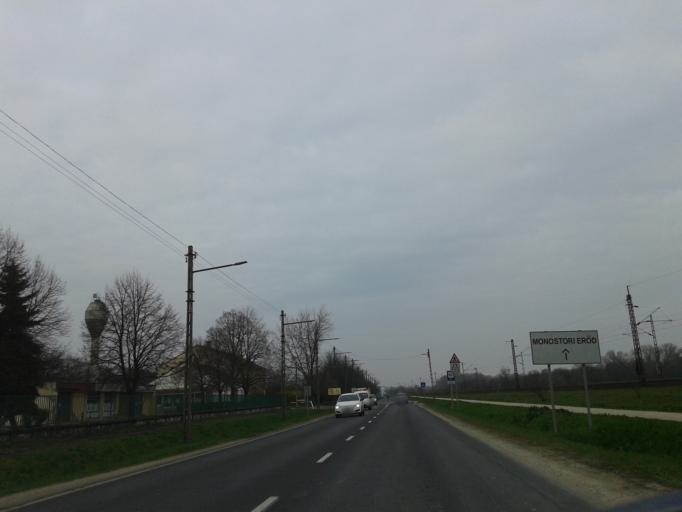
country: HU
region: Komarom-Esztergom
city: Mocsa
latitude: 47.7335
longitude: 18.1970
